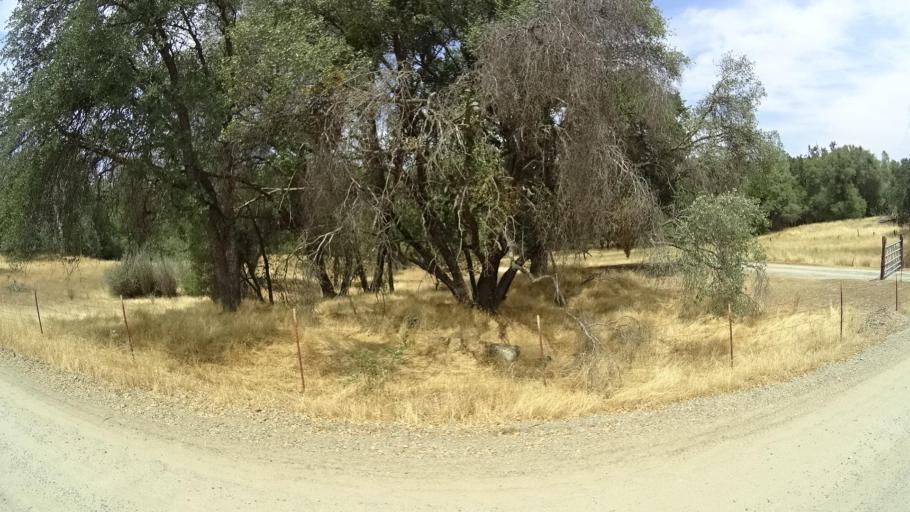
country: US
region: California
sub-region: Madera County
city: Ahwahnee
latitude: 37.4069
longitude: -119.8250
